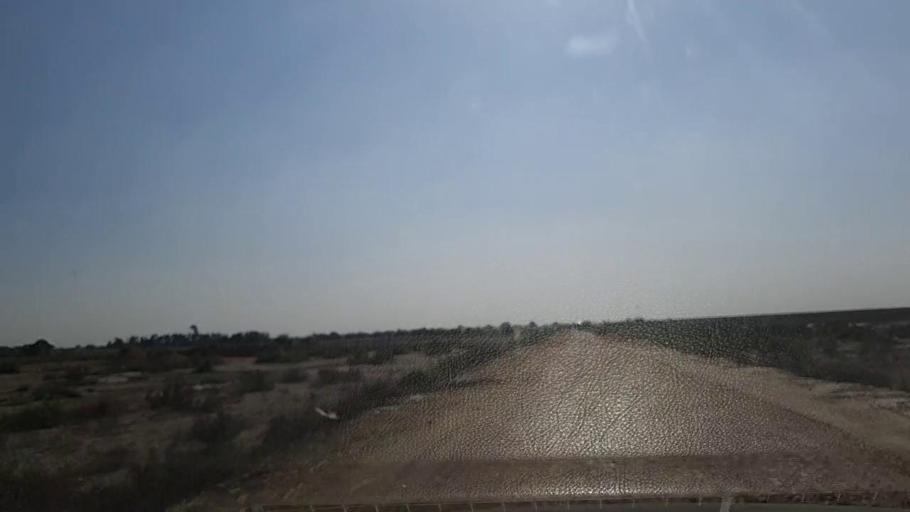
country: PK
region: Sindh
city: Daro Mehar
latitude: 24.7612
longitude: 68.0642
